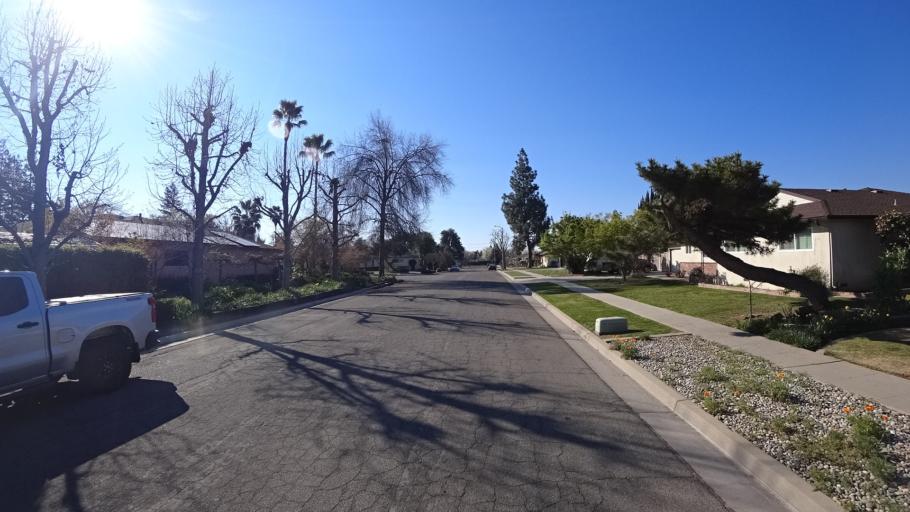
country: US
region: California
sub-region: Fresno County
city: Clovis
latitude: 36.8323
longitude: -119.7660
